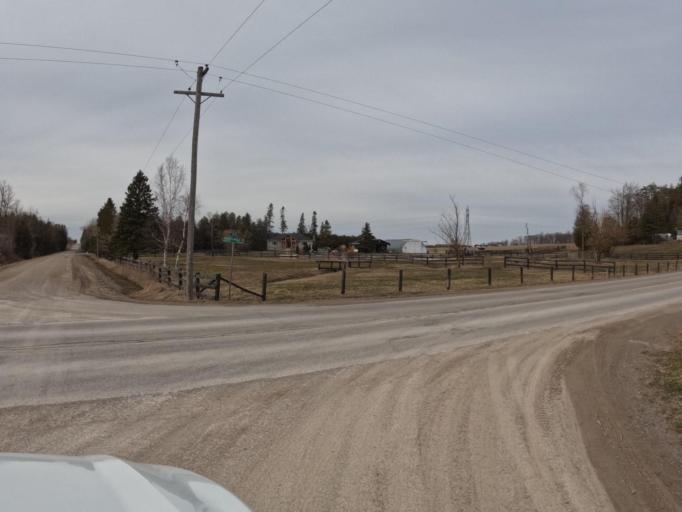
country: CA
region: Ontario
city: Shelburne
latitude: 43.9428
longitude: -80.2605
